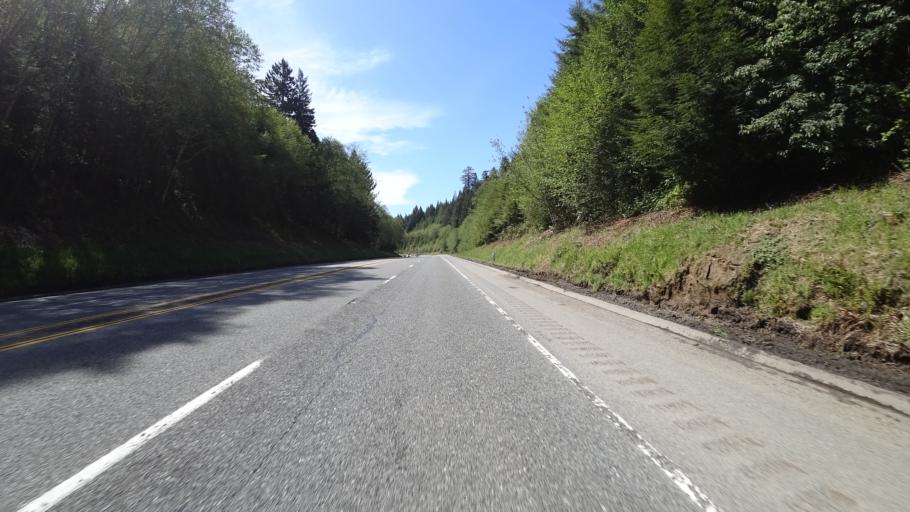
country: US
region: California
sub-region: Del Norte County
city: Bertsch-Oceanview
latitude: 41.4382
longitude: -124.0218
